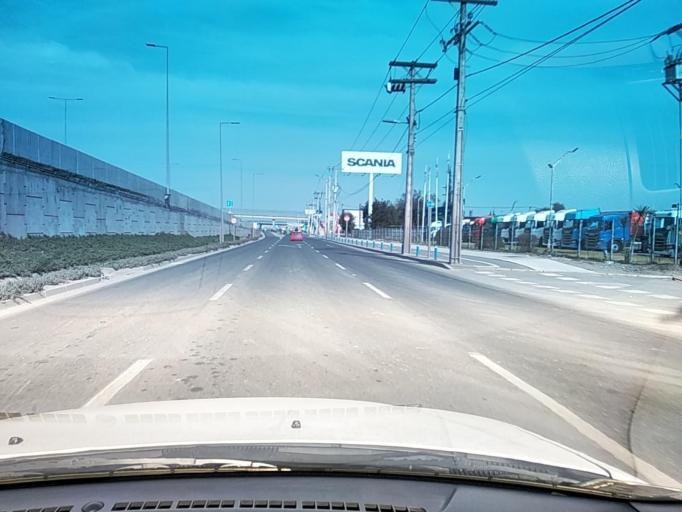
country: CL
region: Santiago Metropolitan
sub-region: Provincia de Chacabuco
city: Chicureo Abajo
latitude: -33.3294
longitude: -70.7171
